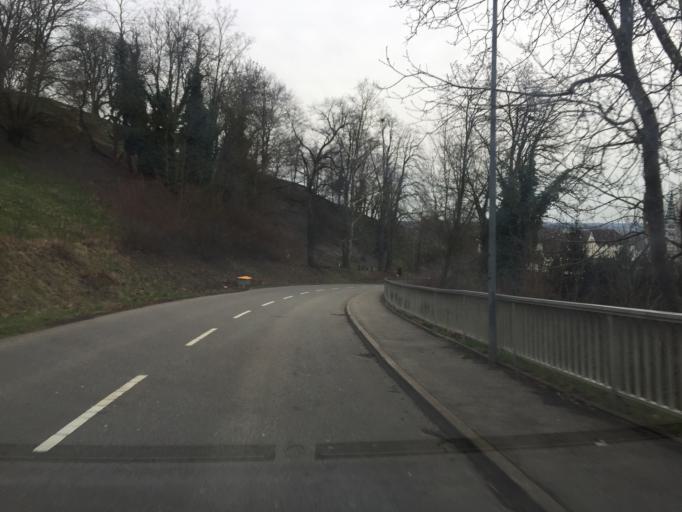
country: CH
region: Thurgau
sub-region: Frauenfeld District
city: Diessenhofen
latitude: 47.6935
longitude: 8.7504
